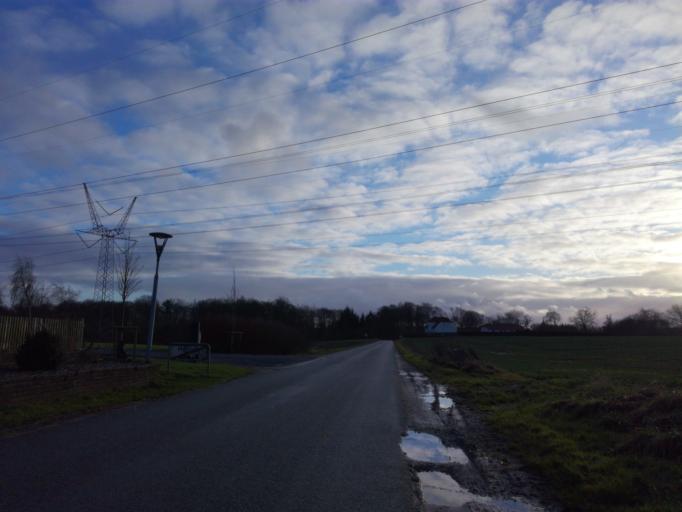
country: DK
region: South Denmark
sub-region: Fredericia Kommune
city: Taulov
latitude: 55.5551
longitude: 9.6025
